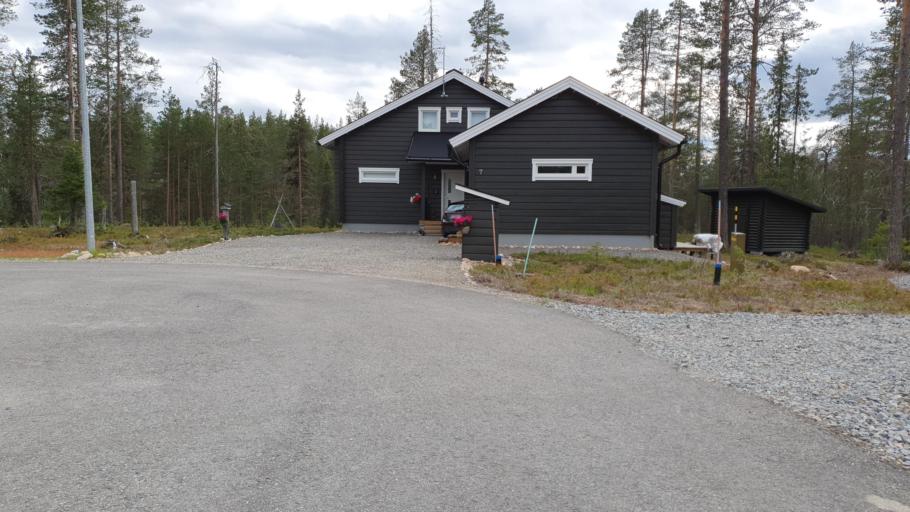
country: FI
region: Lapland
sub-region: Tunturi-Lappi
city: Kolari
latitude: 67.5978
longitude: 24.1314
